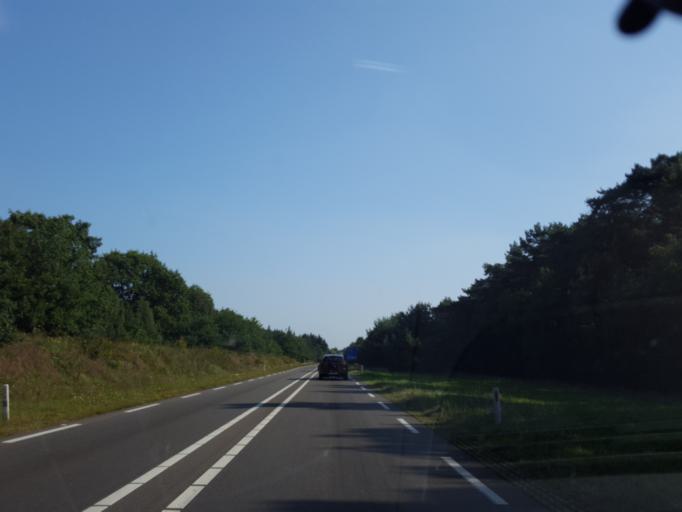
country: NL
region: North Brabant
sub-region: Gemeente Helmond
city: Helmond
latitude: 51.4845
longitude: 5.7108
